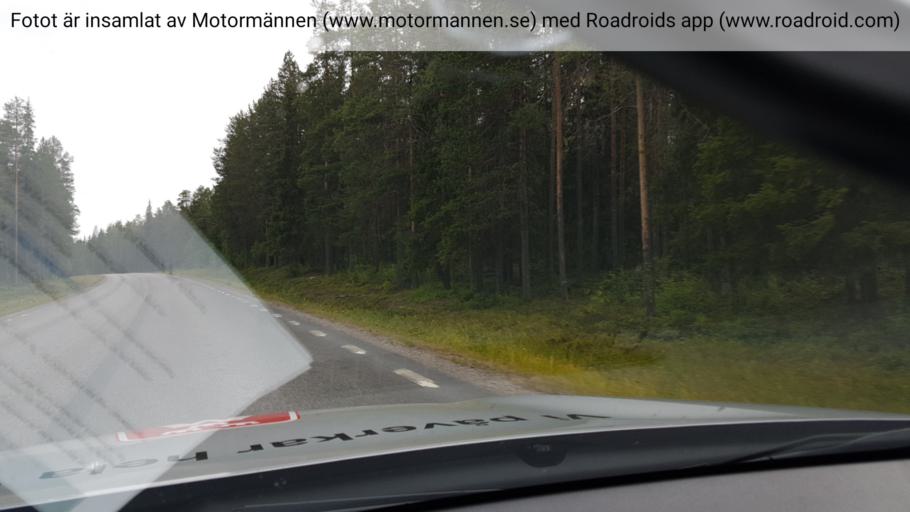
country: SE
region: Norrbotten
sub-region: Overkalix Kommun
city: OEverkalix
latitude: 66.2445
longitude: 22.8036
